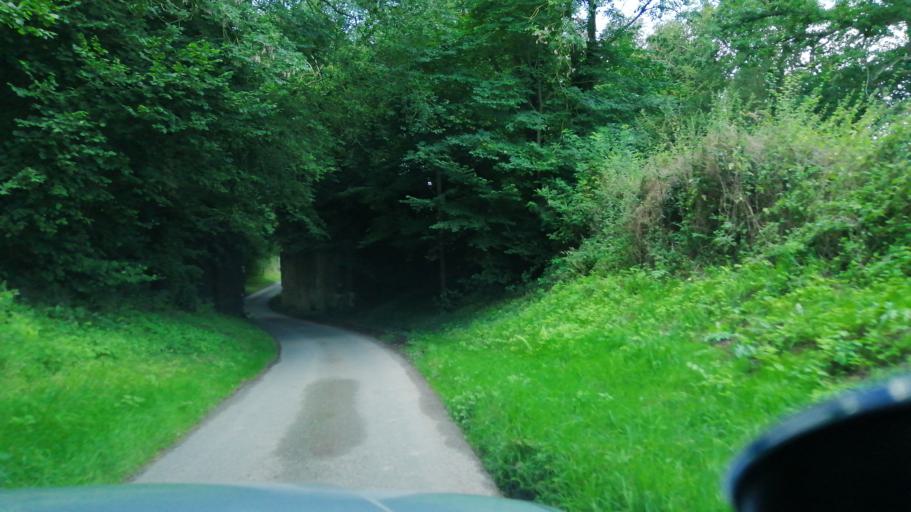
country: GB
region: England
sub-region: Herefordshire
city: Kinnersley
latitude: 52.1229
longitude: -2.9140
